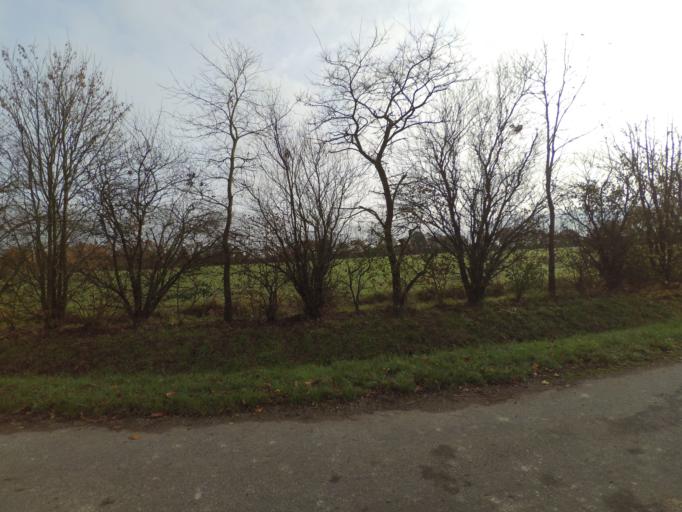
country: FR
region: Pays de la Loire
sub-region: Departement de la Loire-Atlantique
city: La Planche
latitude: 47.0187
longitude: -1.4074
